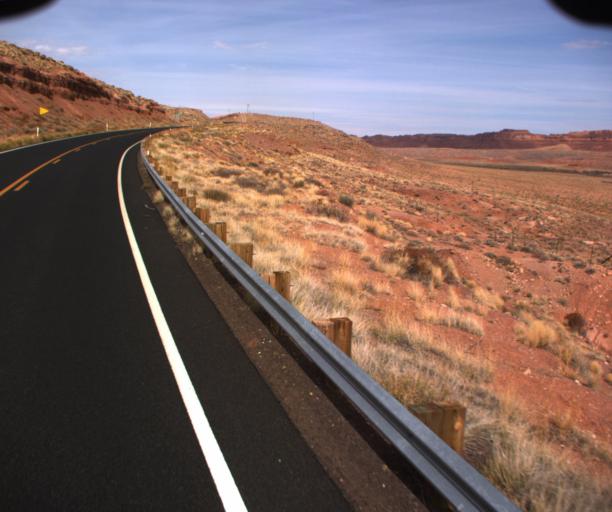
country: US
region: Arizona
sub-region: Apache County
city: Many Farms
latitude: 36.5462
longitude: -109.5304
